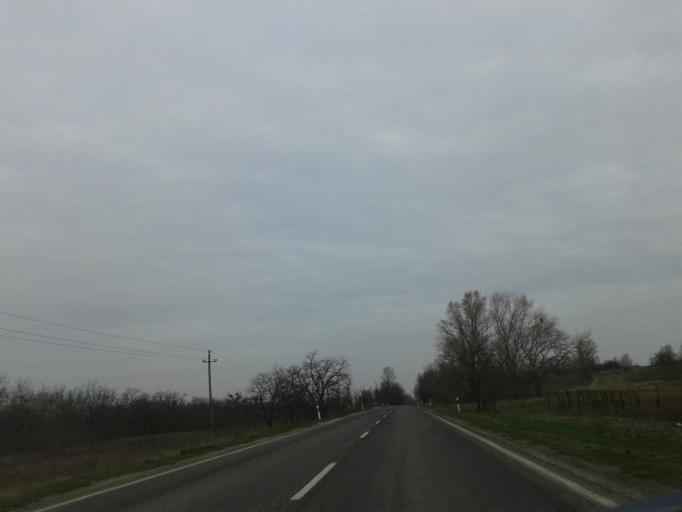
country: HU
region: Komarom-Esztergom
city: Szomod
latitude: 47.6817
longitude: 18.3154
